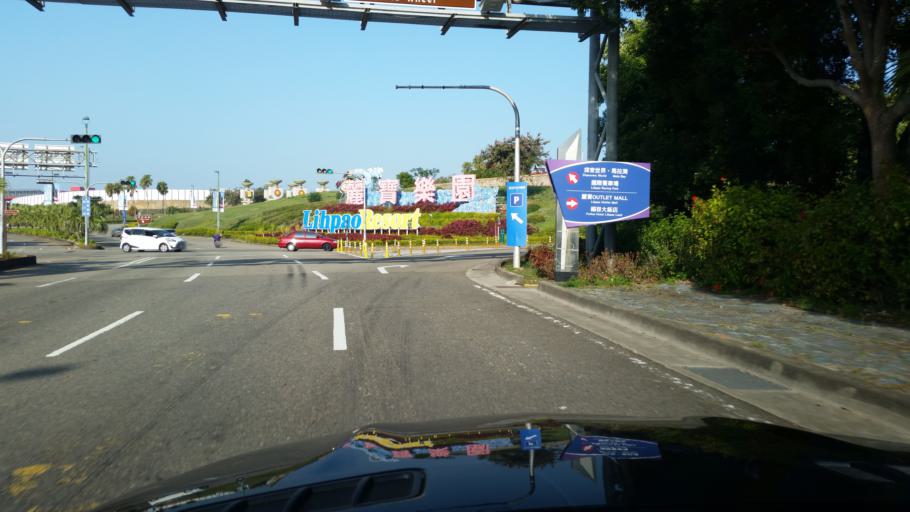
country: TW
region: Taiwan
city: Fengyuan
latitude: 24.3178
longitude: 120.6941
